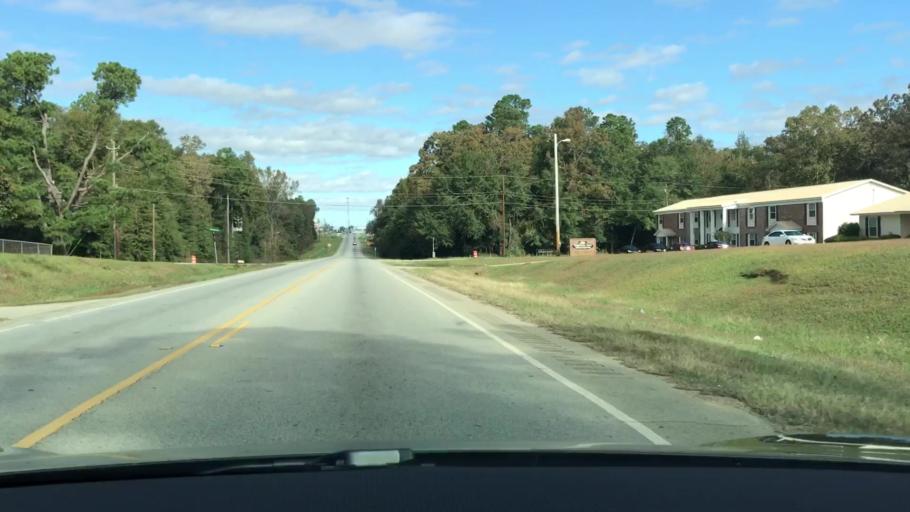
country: US
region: Georgia
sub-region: Jefferson County
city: Louisville
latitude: 32.9989
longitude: -82.3948
